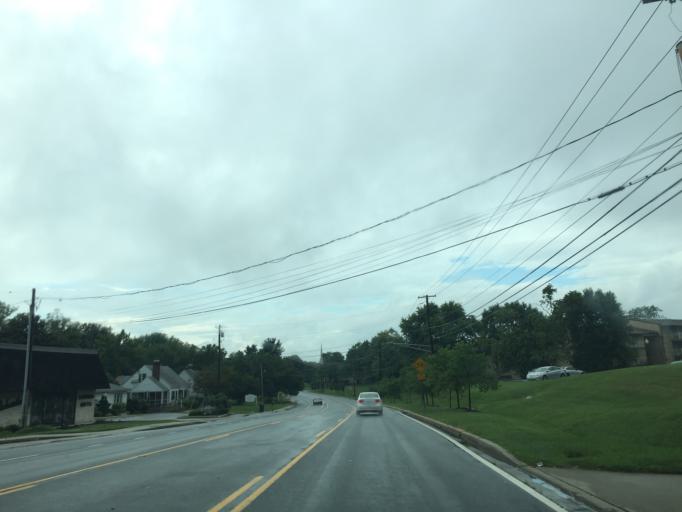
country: US
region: Maryland
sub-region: Harford County
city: South Bel Air
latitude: 39.5273
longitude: -76.3401
